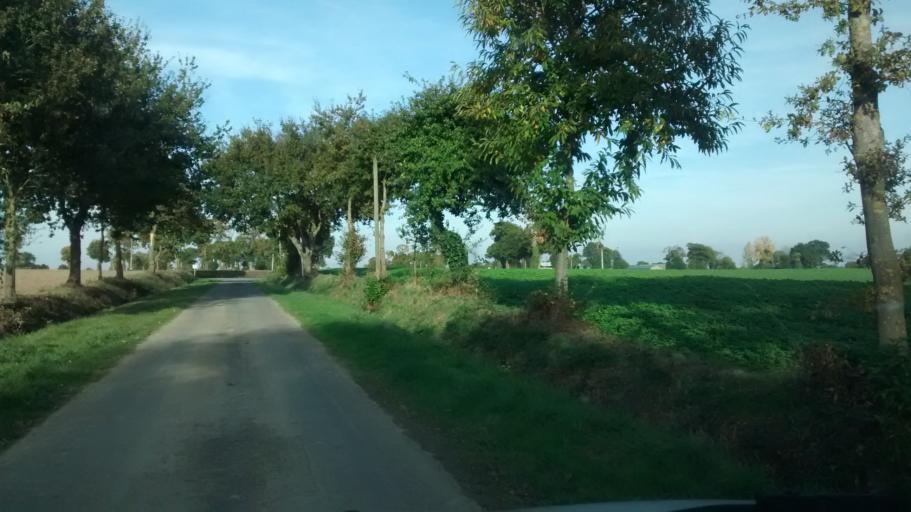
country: FR
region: Brittany
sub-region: Departement d'Ille-et-Vilaine
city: Melesse
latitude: 48.1928
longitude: -1.6805
